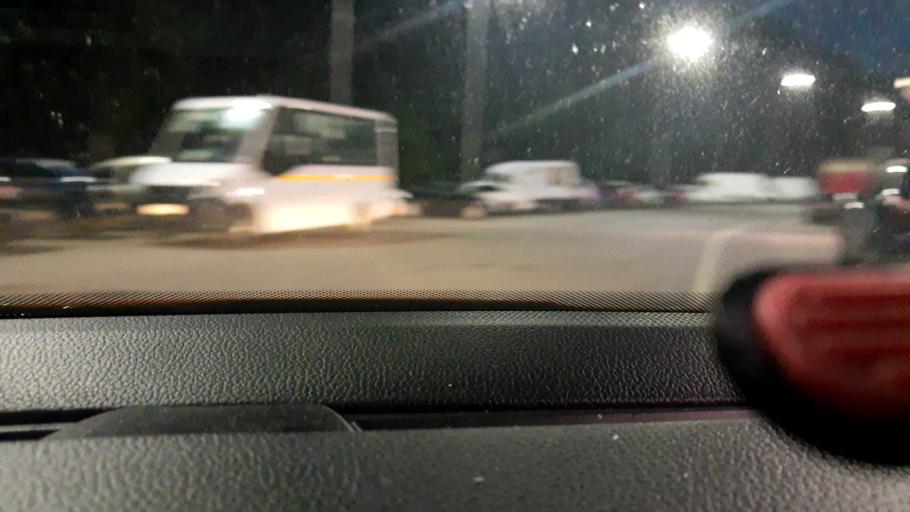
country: RU
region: Moskovskaya
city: Pirogovskiy
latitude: 55.9552
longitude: 37.6856
